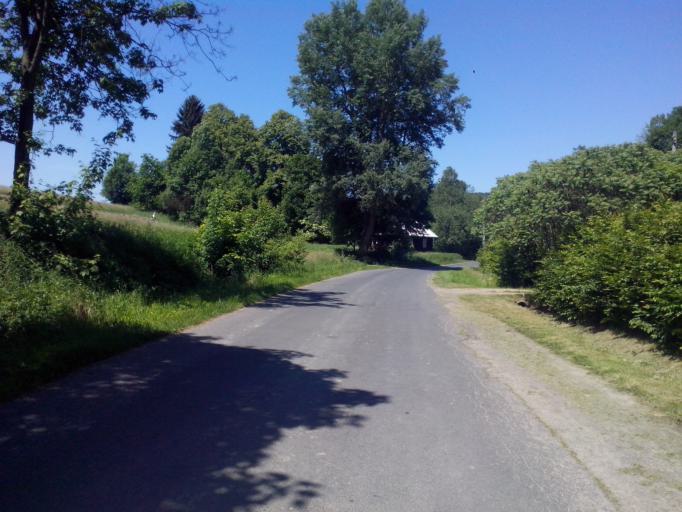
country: PL
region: Subcarpathian Voivodeship
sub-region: Powiat krosnienski
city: Wojaszowka
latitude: 49.7986
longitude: 21.7023
